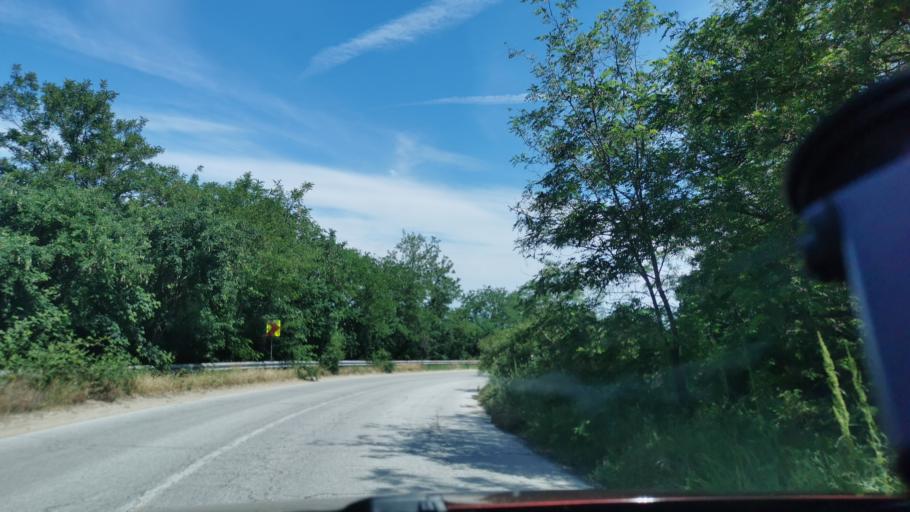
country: BG
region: Khaskovo
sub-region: Obshtina Topolovgrad
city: Topolovgrad
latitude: 42.0306
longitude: 26.1450
